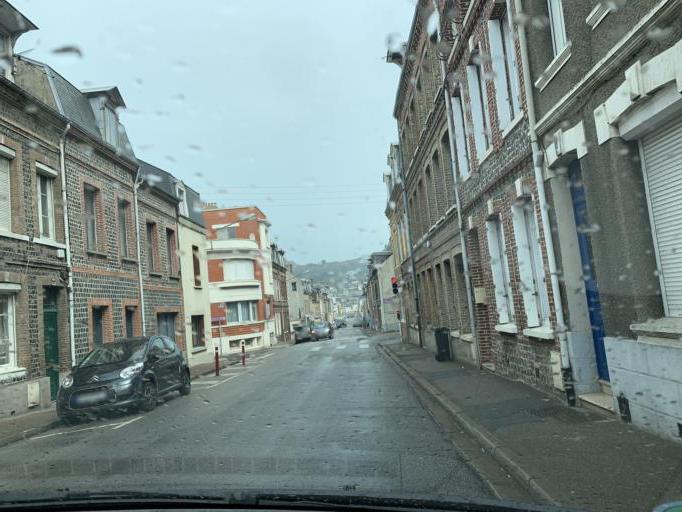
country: FR
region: Haute-Normandie
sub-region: Departement de la Seine-Maritime
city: Fecamp
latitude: 49.7583
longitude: 0.3643
